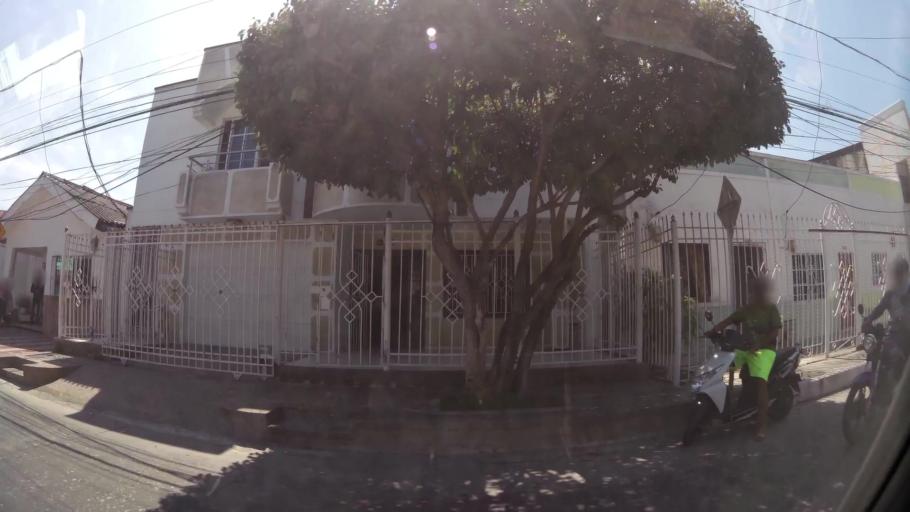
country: CO
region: Atlantico
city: Barranquilla
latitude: 10.9646
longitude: -74.8047
